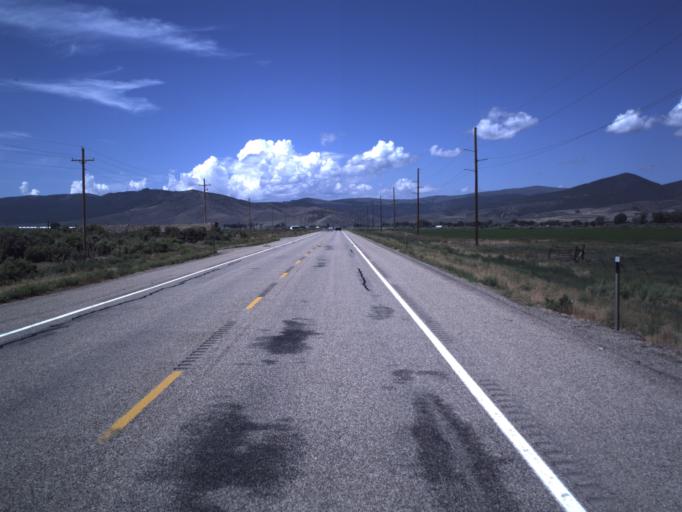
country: US
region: Utah
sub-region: Piute County
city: Junction
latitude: 38.1854
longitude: -112.2430
